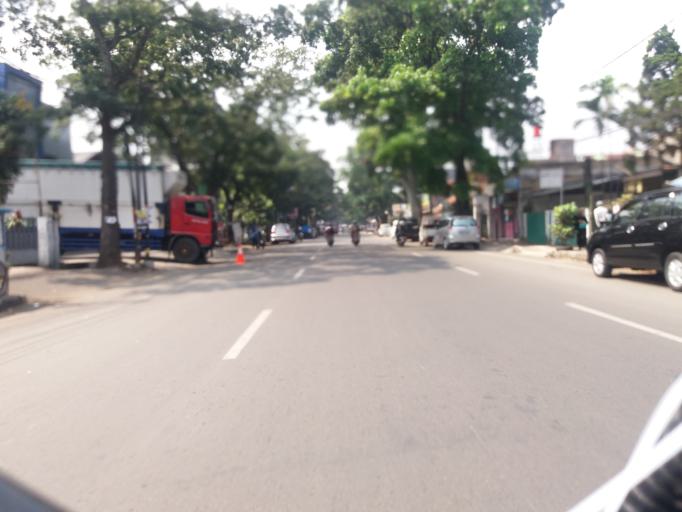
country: ID
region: West Java
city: Bandung
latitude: -6.9145
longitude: 107.5812
